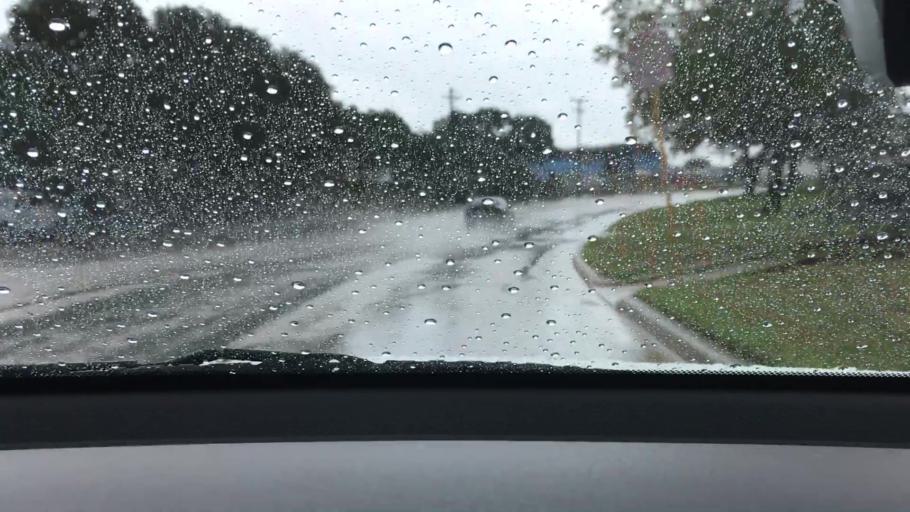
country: US
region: Texas
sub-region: Bexar County
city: Alamo Heights
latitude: 29.5354
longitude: -98.4475
